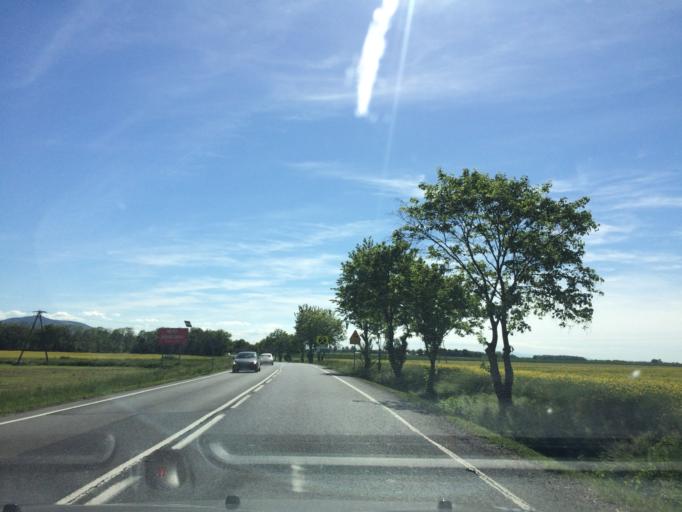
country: PL
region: Lower Silesian Voivodeship
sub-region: Powiat wroclawski
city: Gniechowice
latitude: 50.9634
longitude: 16.7927
